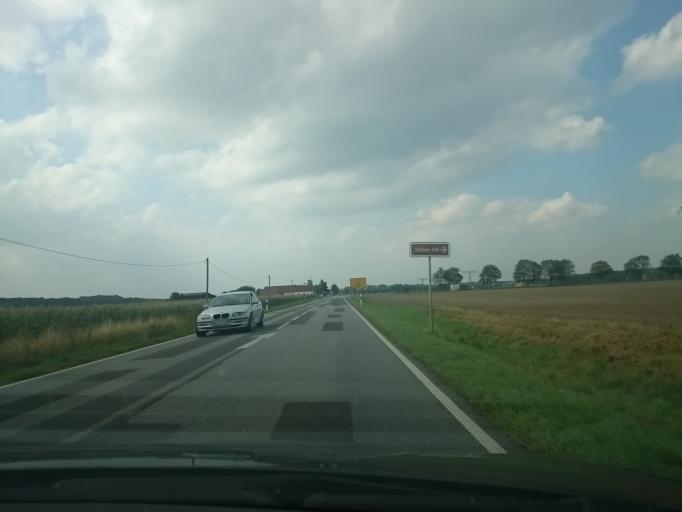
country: DE
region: Mecklenburg-Vorpommern
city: Ferdinandshof
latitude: 53.7069
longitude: 13.8508
